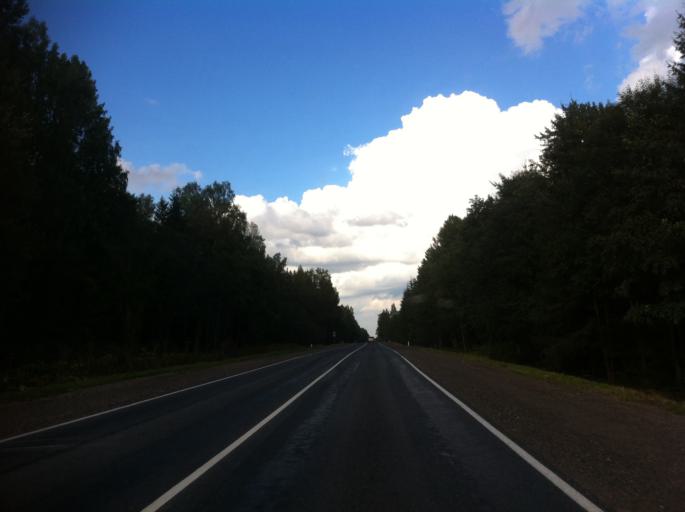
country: RU
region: Pskov
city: Strugi-Krasnyye
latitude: 58.1938
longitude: 29.2827
